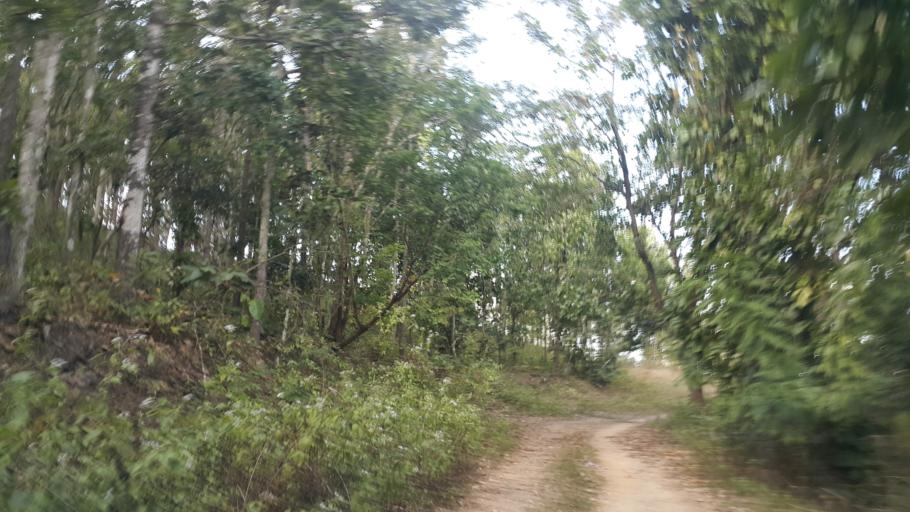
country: TH
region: Lamphun
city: Ban Thi
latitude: 18.5842
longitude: 99.1603
